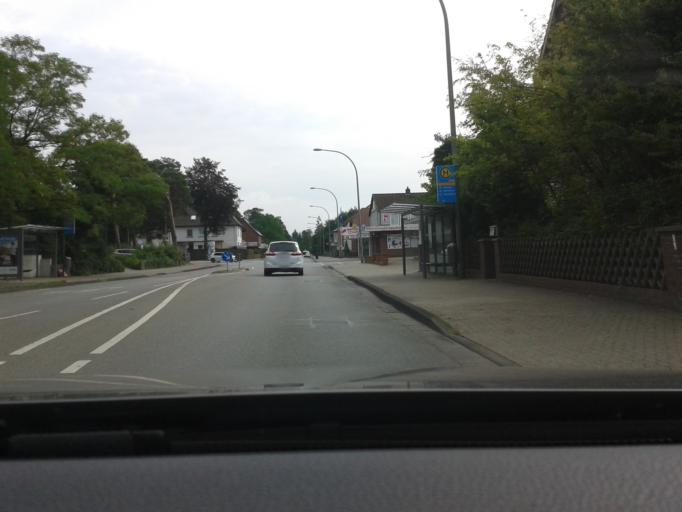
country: DE
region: Lower Saxony
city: Gifhorn
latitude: 52.4799
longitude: 10.5517
